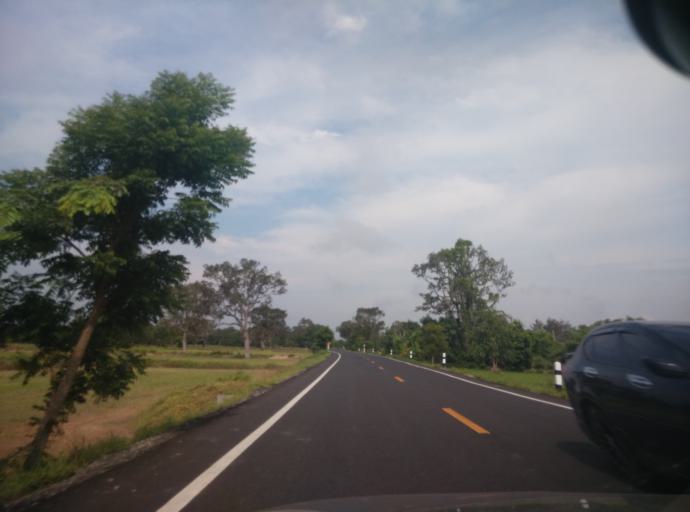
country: TH
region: Sisaket
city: Si Sa Ket
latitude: 15.1221
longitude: 104.2369
